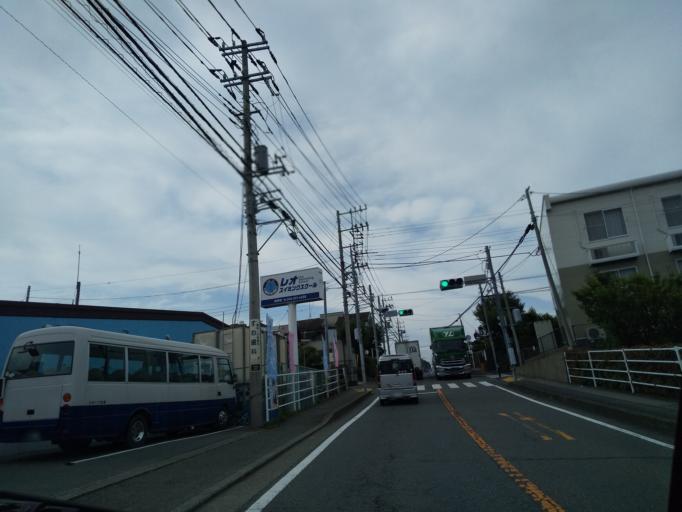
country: JP
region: Kanagawa
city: Atsugi
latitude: 35.4750
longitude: 139.3406
